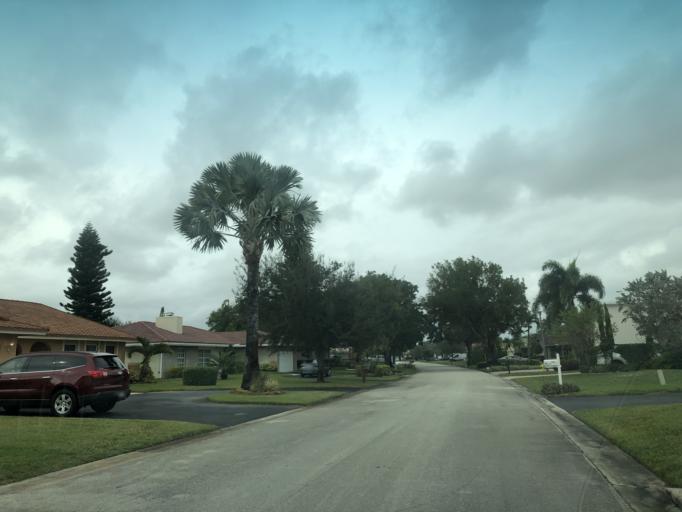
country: US
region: Florida
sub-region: Broward County
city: North Lauderdale
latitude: 26.2413
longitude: -80.2367
